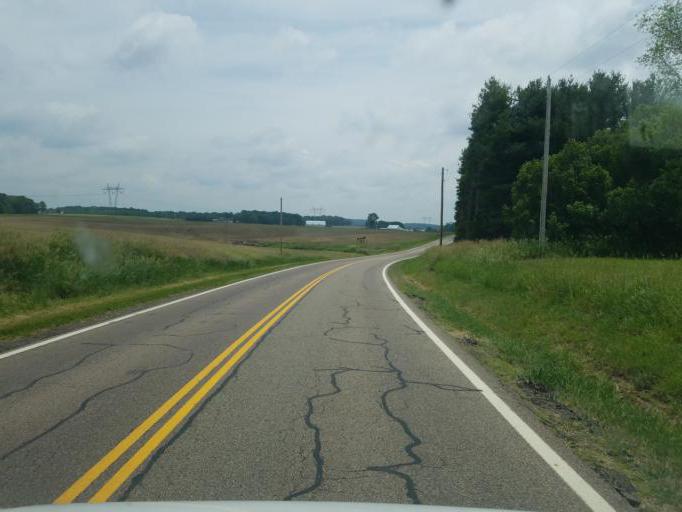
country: US
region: Ohio
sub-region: Knox County
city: Gambier
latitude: 40.3551
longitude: -82.3204
